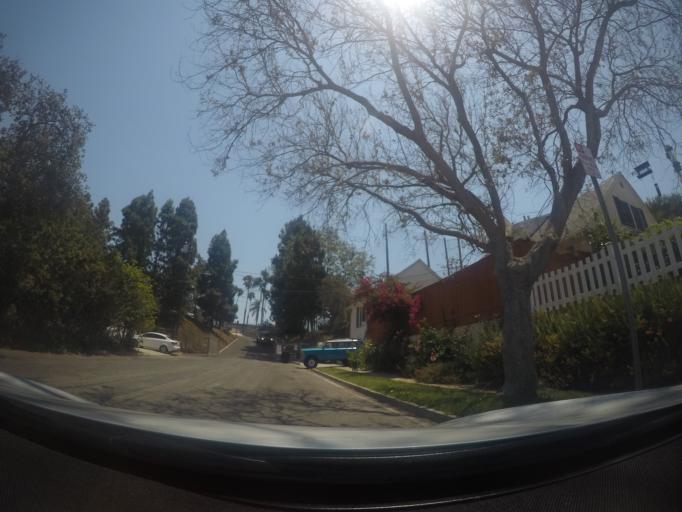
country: US
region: California
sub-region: Los Angeles County
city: Torrance
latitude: 33.8220
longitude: -118.3665
